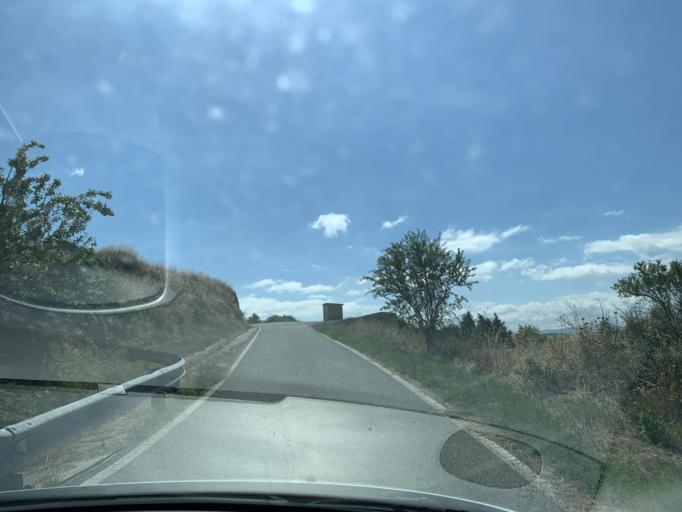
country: ES
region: Catalonia
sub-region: Provincia de Tarragona
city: Conesa
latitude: 41.5424
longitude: 1.2967
